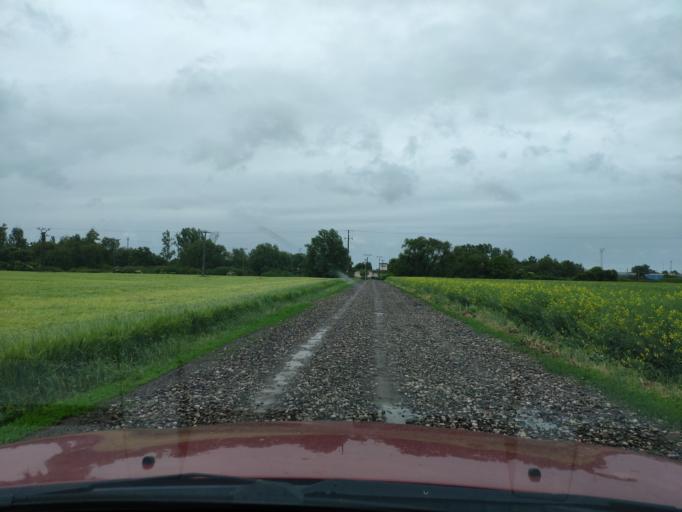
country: SK
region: Kosicky
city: Cierna nad Tisou
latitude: 48.4262
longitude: 22.0817
